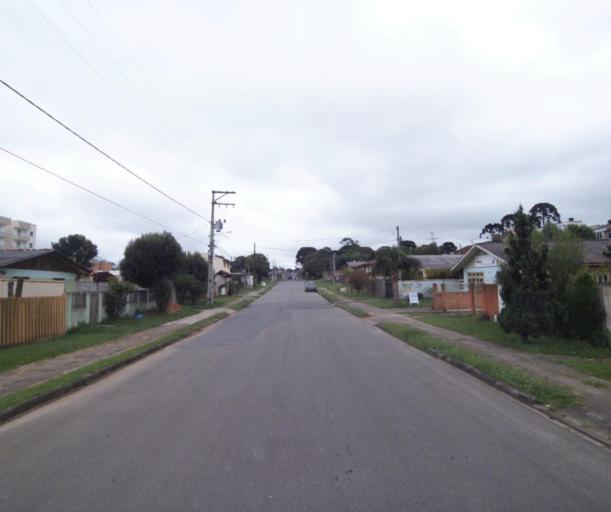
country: BR
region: Parana
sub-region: Quatro Barras
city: Quatro Barras
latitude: -25.3633
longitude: -49.1066
